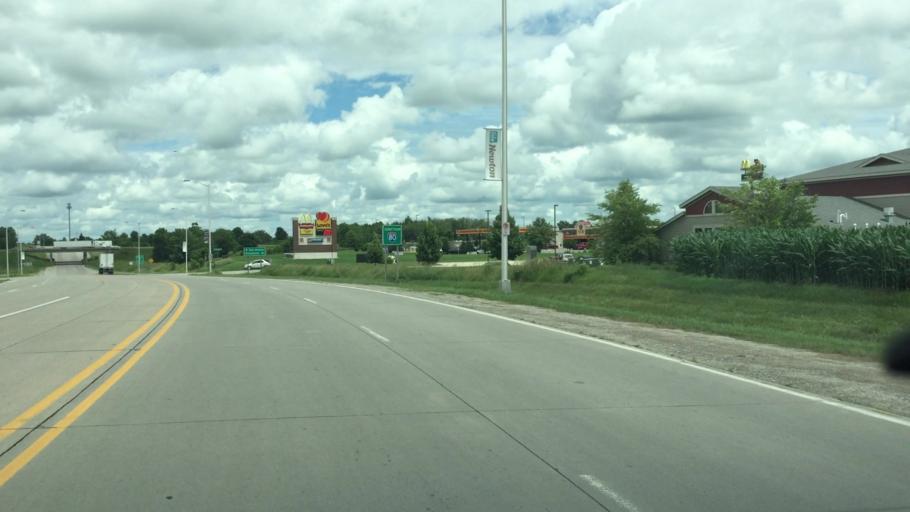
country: US
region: Iowa
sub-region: Jasper County
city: Newton
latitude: 41.6783
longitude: -92.9999
